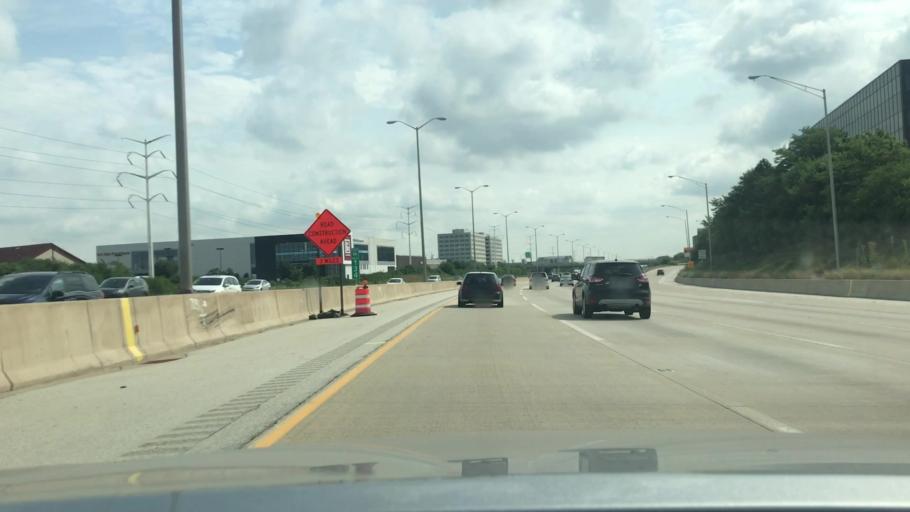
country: US
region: Illinois
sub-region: DuPage County
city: Downers Grove
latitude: 41.8296
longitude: -88.0168
